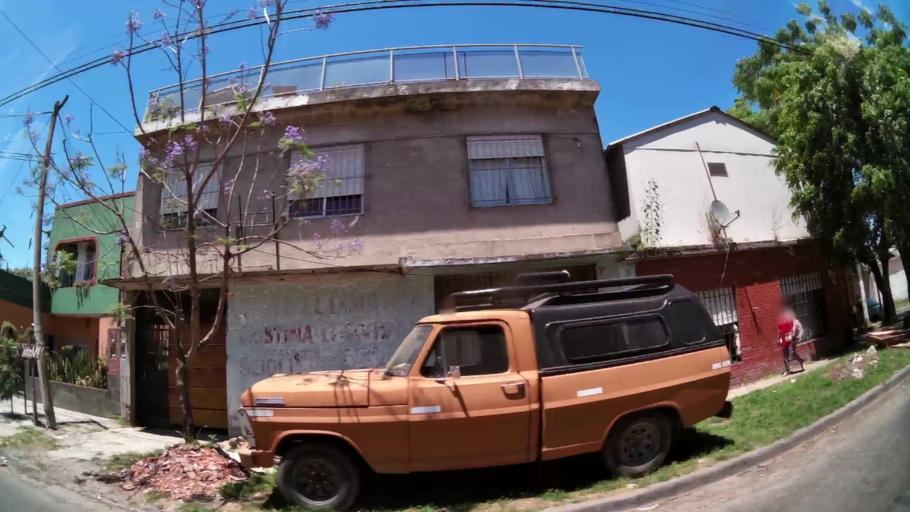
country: AR
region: Buenos Aires
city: Hurlingham
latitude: -34.5069
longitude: -58.7078
